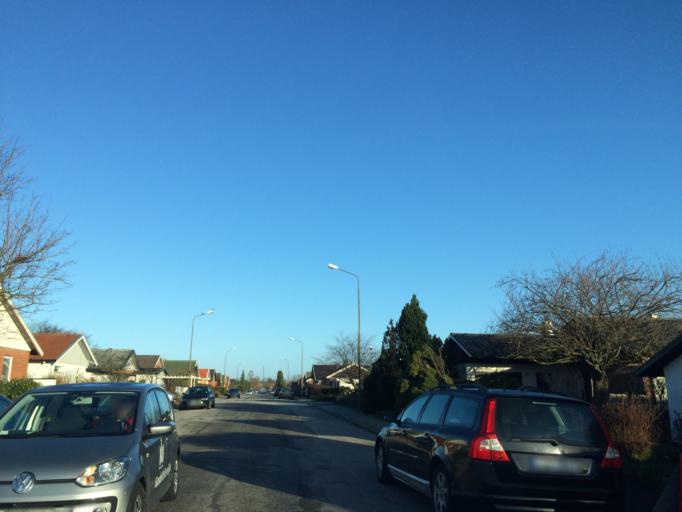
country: SE
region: Skane
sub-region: Malmo
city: Bunkeflostrand
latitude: 55.5709
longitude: 12.9492
